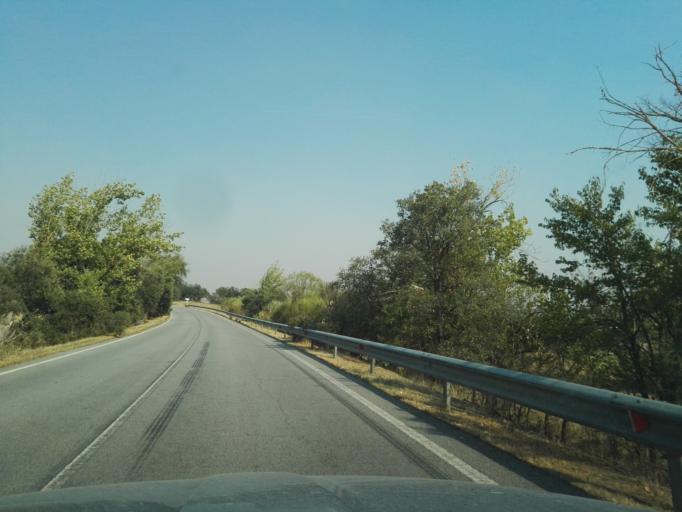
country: PT
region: Portalegre
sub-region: Campo Maior
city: Campo Maior
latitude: 38.9932
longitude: -7.1567
